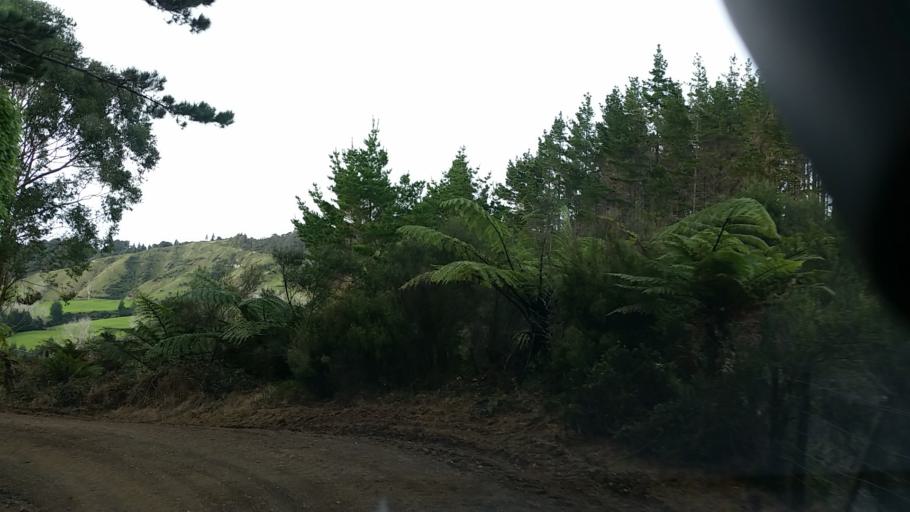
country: NZ
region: Taranaki
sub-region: New Plymouth District
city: Waitara
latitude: -39.0439
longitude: 174.4226
